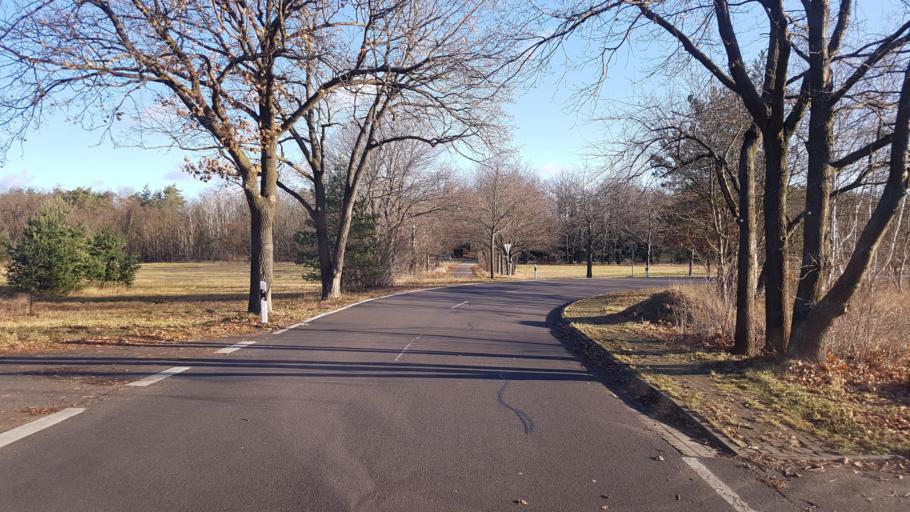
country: DE
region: Brandenburg
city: Heinersbruck
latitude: 51.7500
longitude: 14.5466
